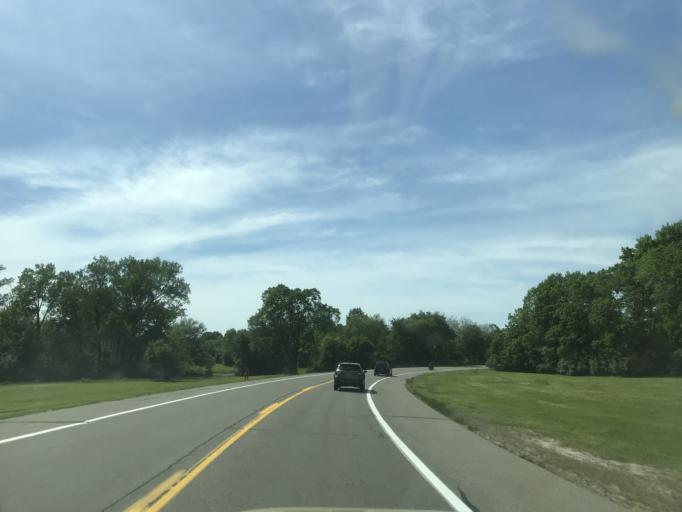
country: US
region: Michigan
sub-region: Wayne County
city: Dearborn Heights
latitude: 42.3474
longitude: -83.2882
